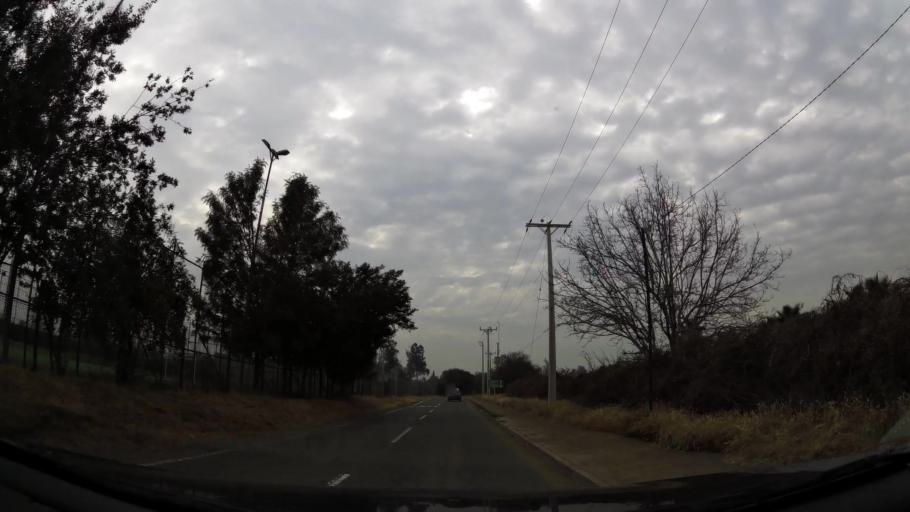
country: CL
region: Santiago Metropolitan
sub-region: Provincia de Chacabuco
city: Chicureo Abajo
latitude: -33.2328
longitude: -70.6912
